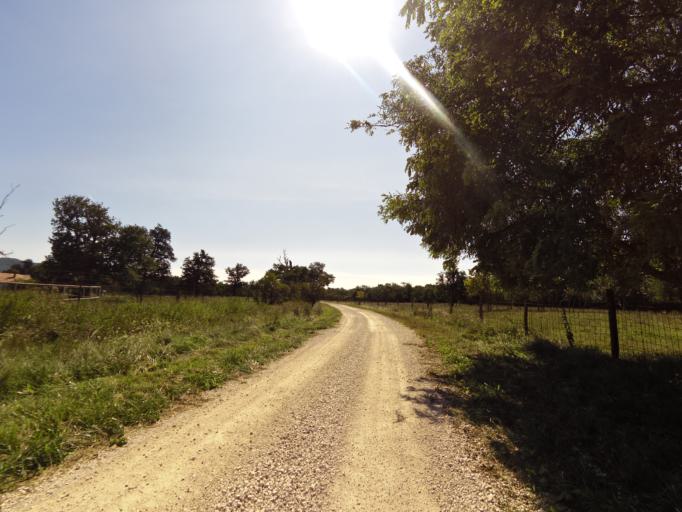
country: HU
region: Veszprem
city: Tapolca
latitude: 46.8409
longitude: 17.3931
